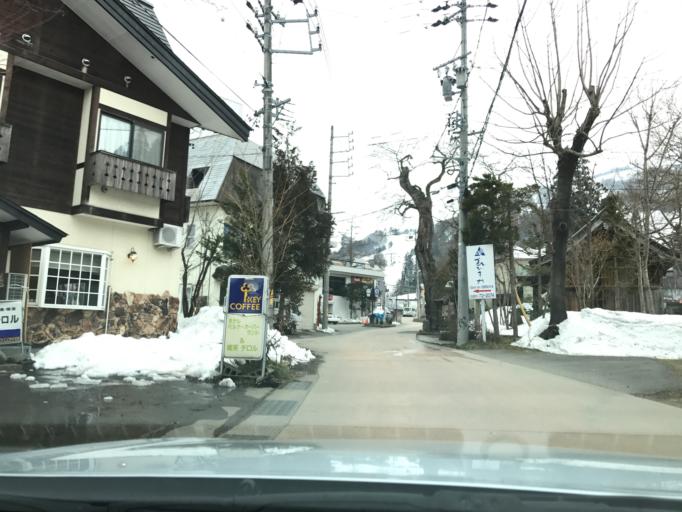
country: JP
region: Nagano
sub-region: Kitaazumi Gun
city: Hakuba
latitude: 36.7008
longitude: 137.8416
